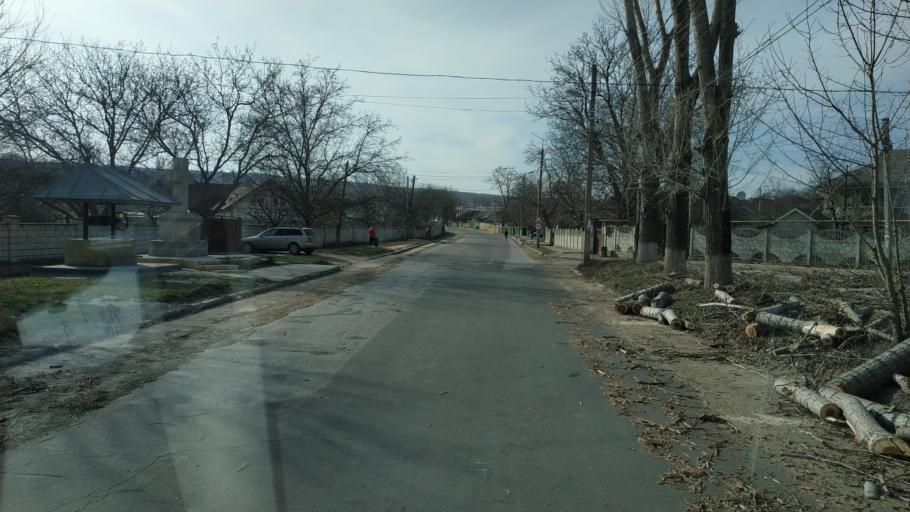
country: MD
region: Chisinau
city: Vatra
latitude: 47.0726
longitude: 28.6928
